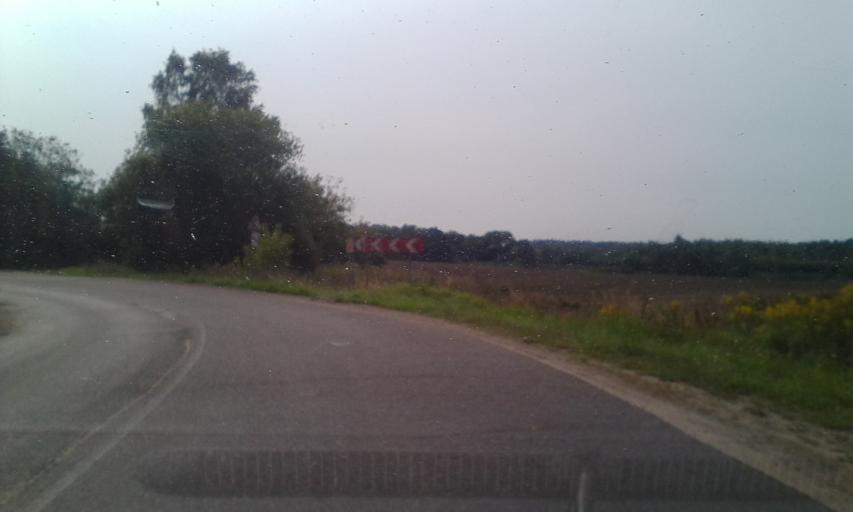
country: BY
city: Michanovichi
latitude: 53.7619
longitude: 27.6722
